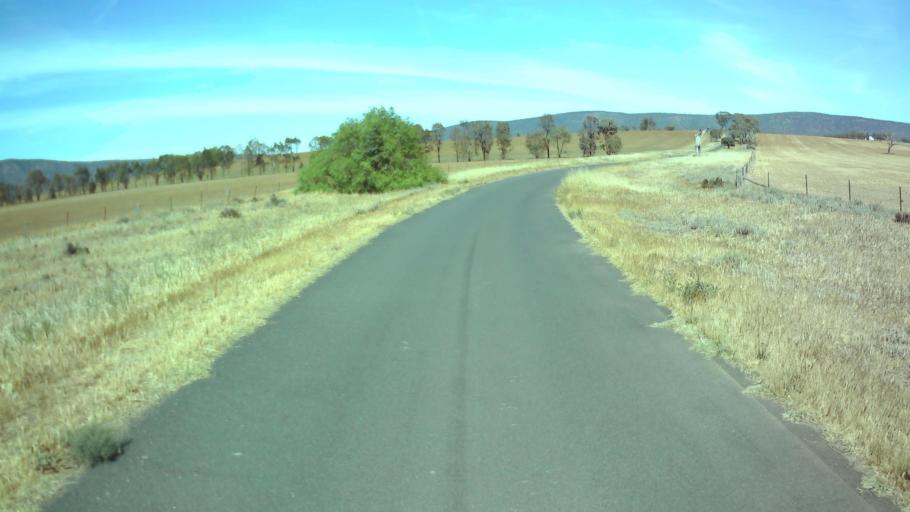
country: AU
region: New South Wales
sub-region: Weddin
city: Grenfell
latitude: -33.9405
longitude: 148.0763
